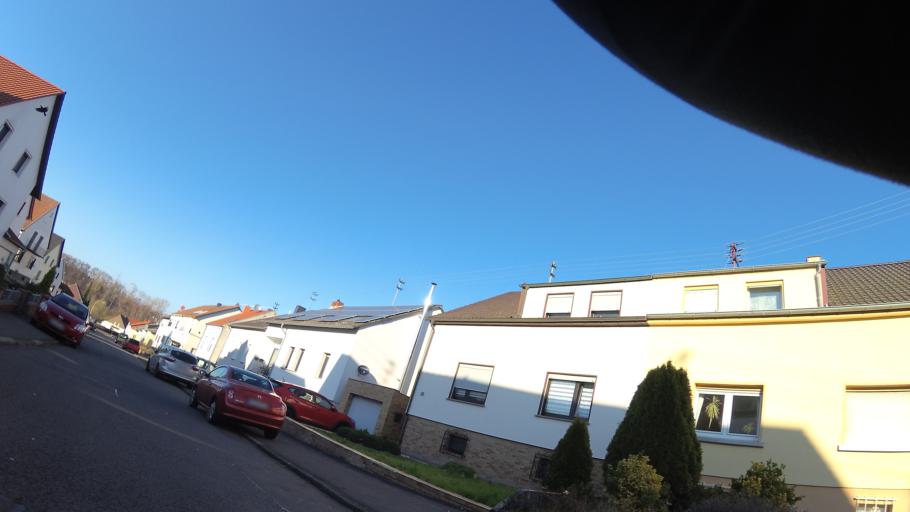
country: DE
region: Saarland
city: Bous
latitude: 49.2920
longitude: 6.8014
